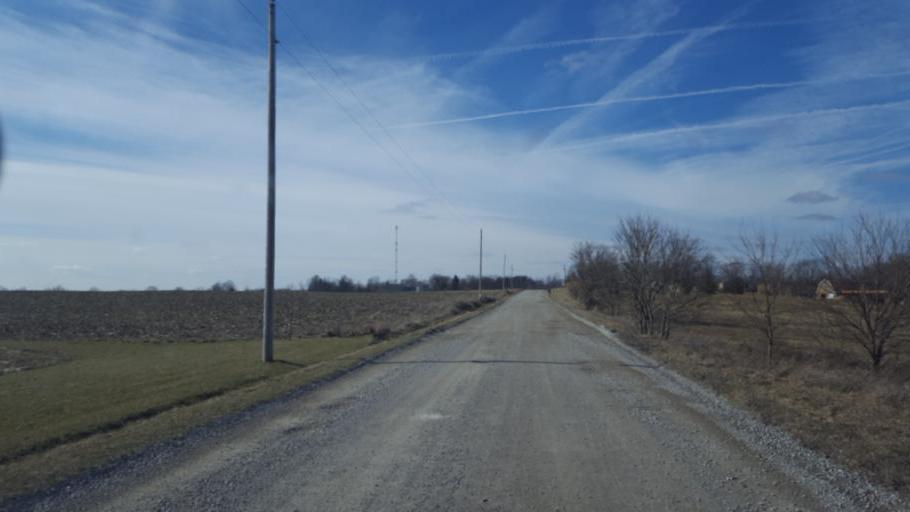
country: US
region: Ohio
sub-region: Knox County
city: Fredericktown
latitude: 40.5000
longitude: -82.6671
